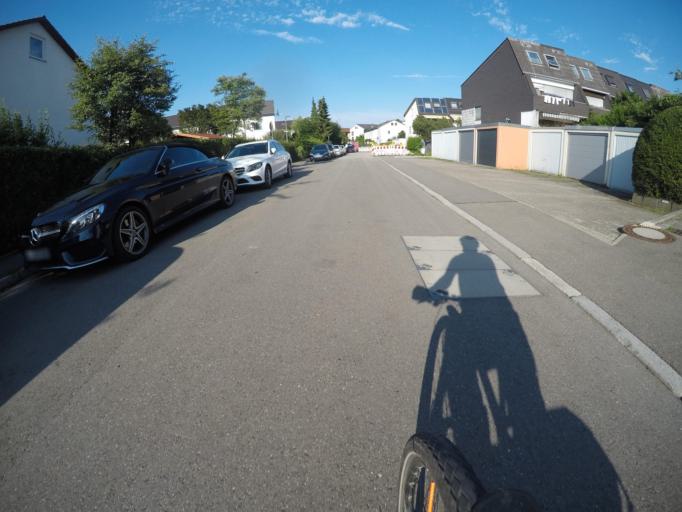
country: DE
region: Baden-Wuerttemberg
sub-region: Regierungsbezirk Stuttgart
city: Boeblingen
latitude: 48.6761
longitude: 8.9973
